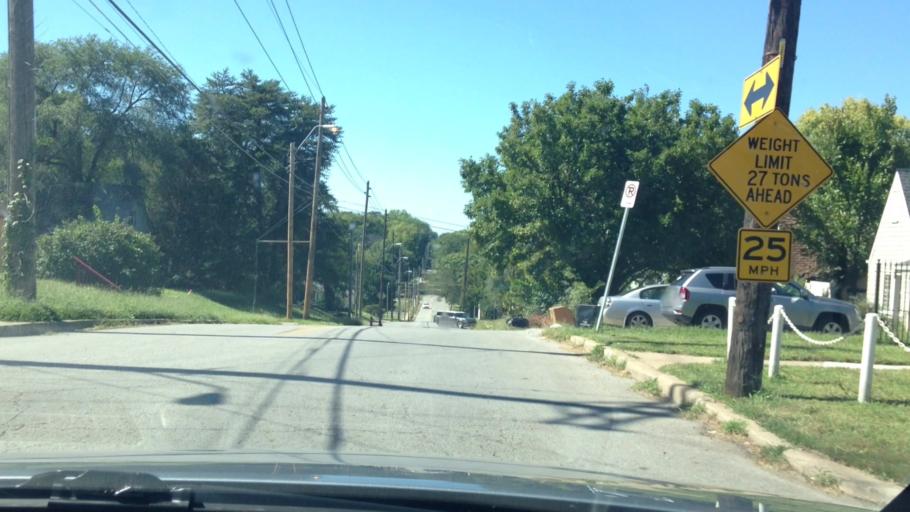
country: US
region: Kansas
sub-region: Johnson County
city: Mission Hills
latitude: 39.0190
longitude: -94.5464
